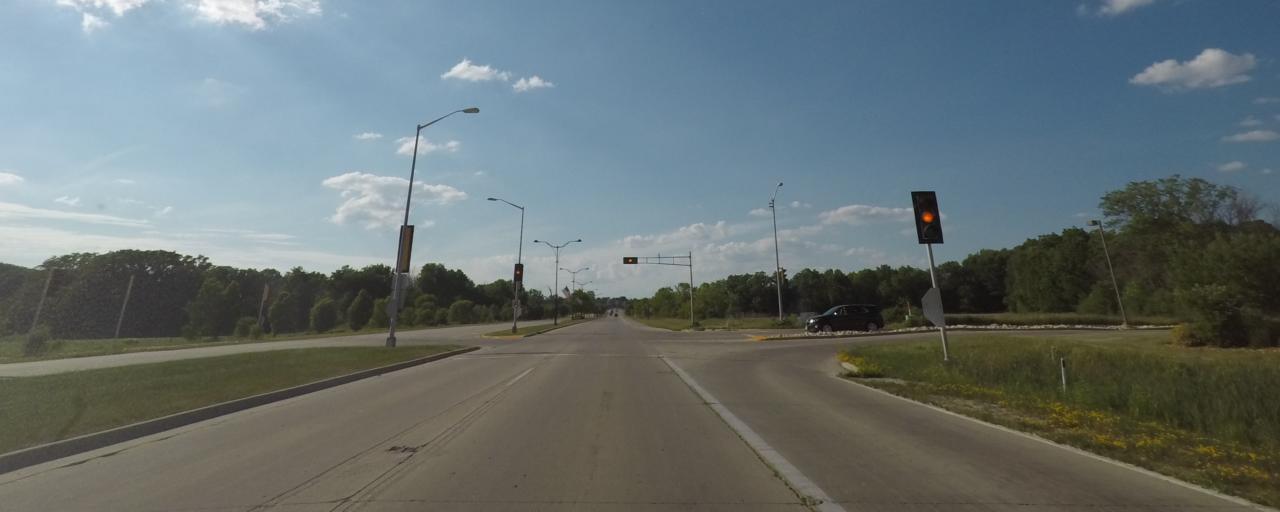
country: US
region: Wisconsin
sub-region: Waukesha County
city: Muskego
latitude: 42.9207
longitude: -88.1097
